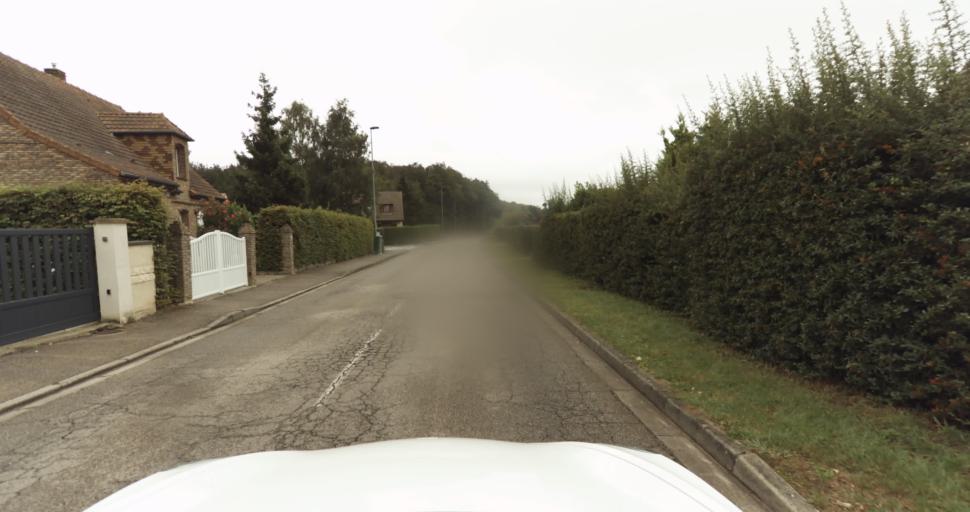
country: FR
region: Haute-Normandie
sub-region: Departement de l'Eure
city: Aviron
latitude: 49.0418
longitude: 1.1371
